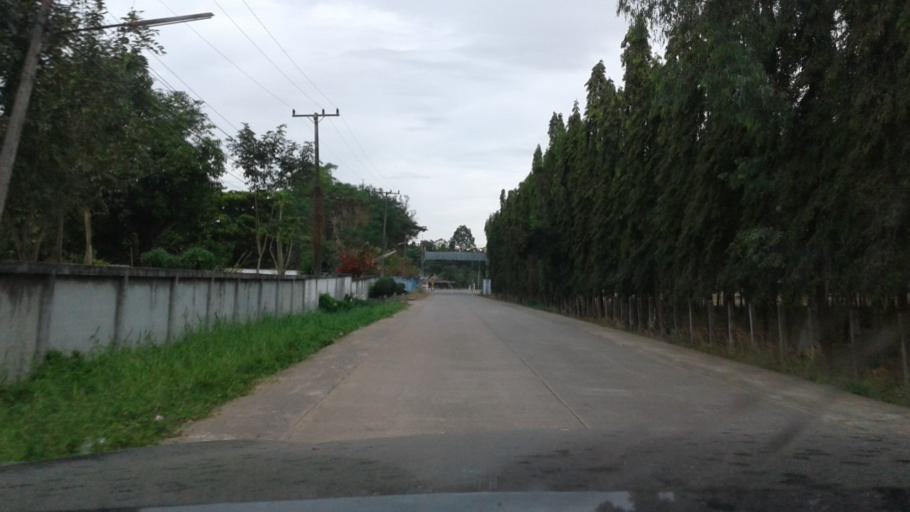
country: TH
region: Changwat Udon Thani
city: Nong Wua So
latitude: 17.2434
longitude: 102.5357
